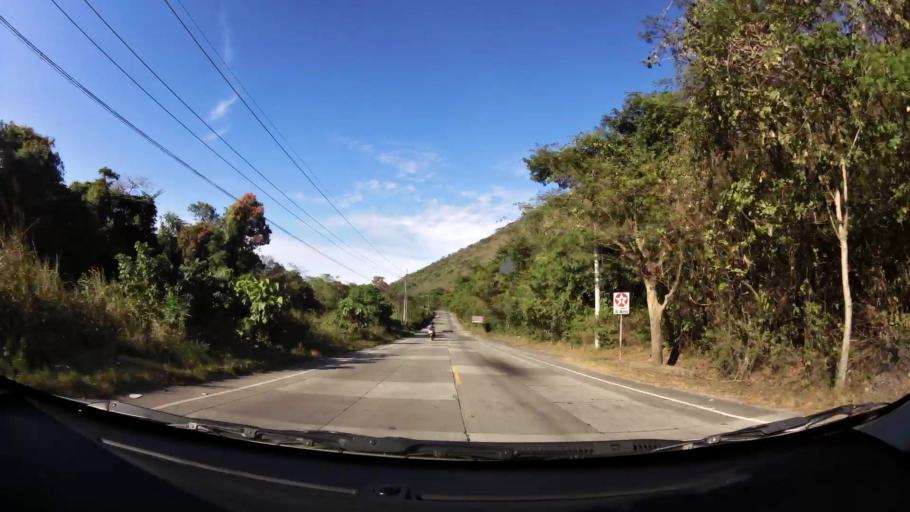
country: SV
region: Santa Ana
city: Metapan
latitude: 14.2600
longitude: -89.4603
